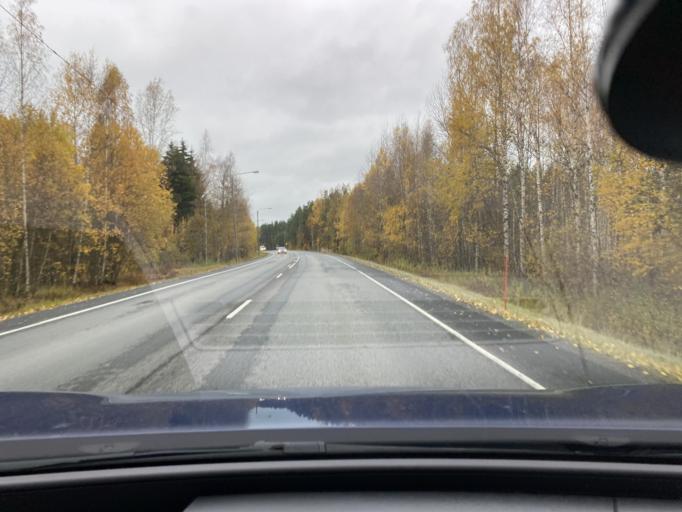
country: FI
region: Satakunta
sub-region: Rauma
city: Rauma
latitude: 61.1327
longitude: 21.5966
